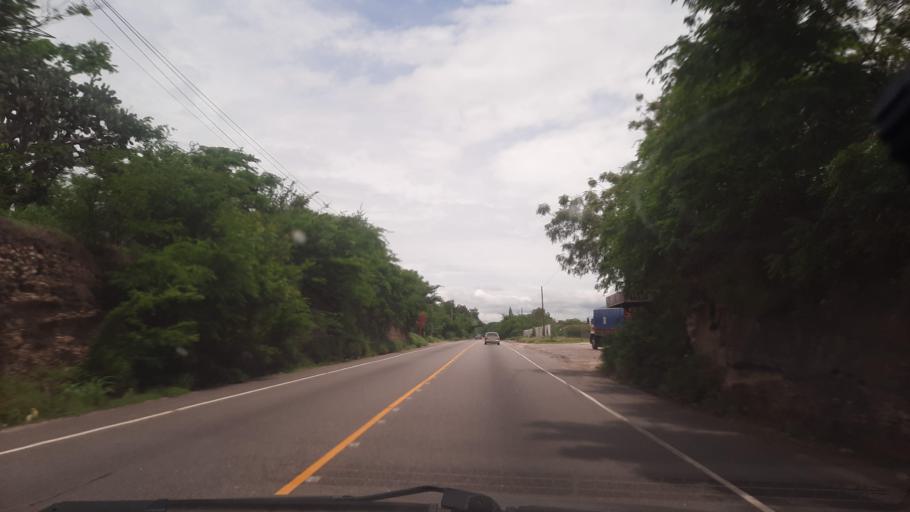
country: GT
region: Zacapa
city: Rio Hondo
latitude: 15.0613
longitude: -89.5376
